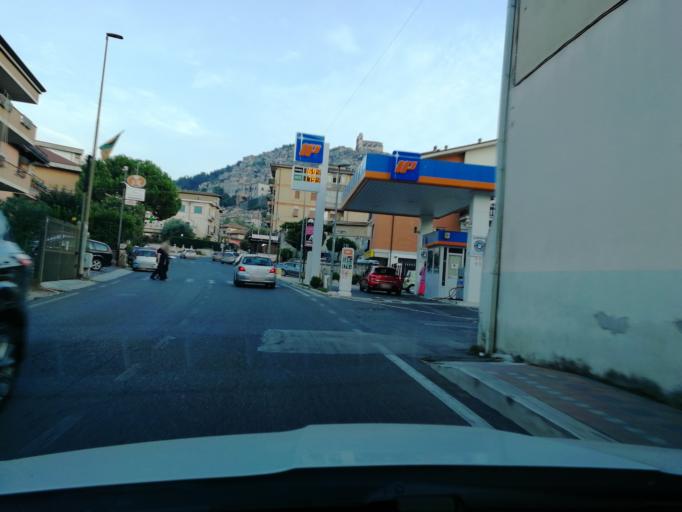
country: IT
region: Latium
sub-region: Citta metropolitana di Roma Capitale
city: Artena
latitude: 41.7431
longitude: 12.9107
